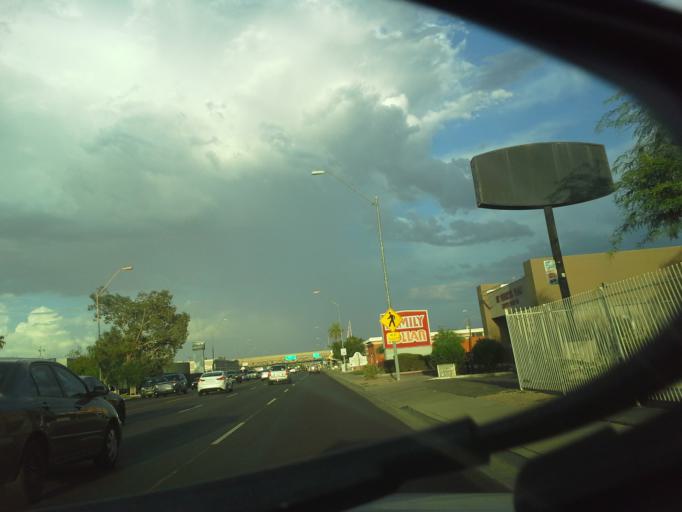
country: US
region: Arizona
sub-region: Maricopa County
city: Phoenix
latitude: 33.4657
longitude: -112.0428
